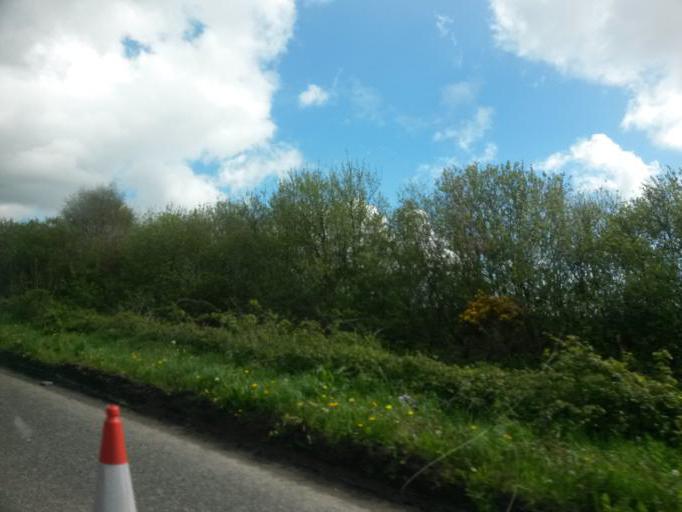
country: IE
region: Leinster
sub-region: Loch Garman
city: Castlebridge
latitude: 52.3787
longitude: -6.5198
